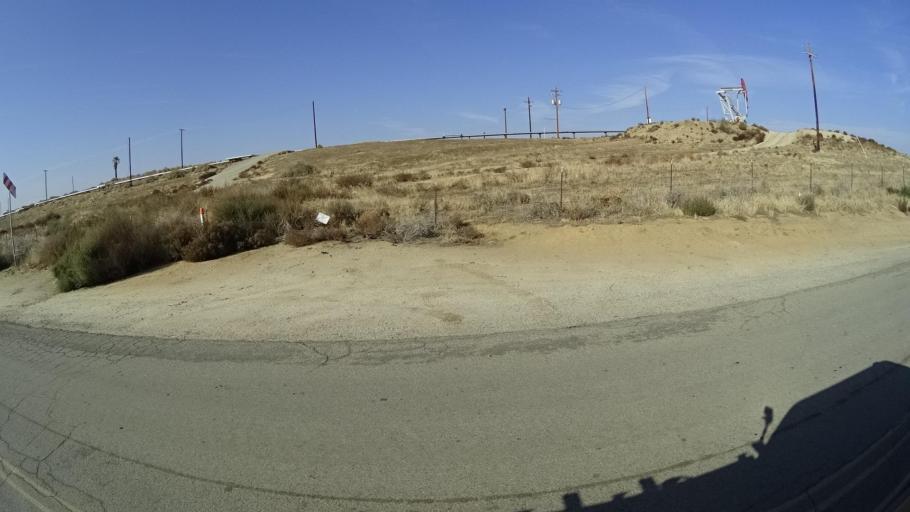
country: US
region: California
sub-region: Kern County
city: Oildale
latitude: 35.4875
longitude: -119.0444
